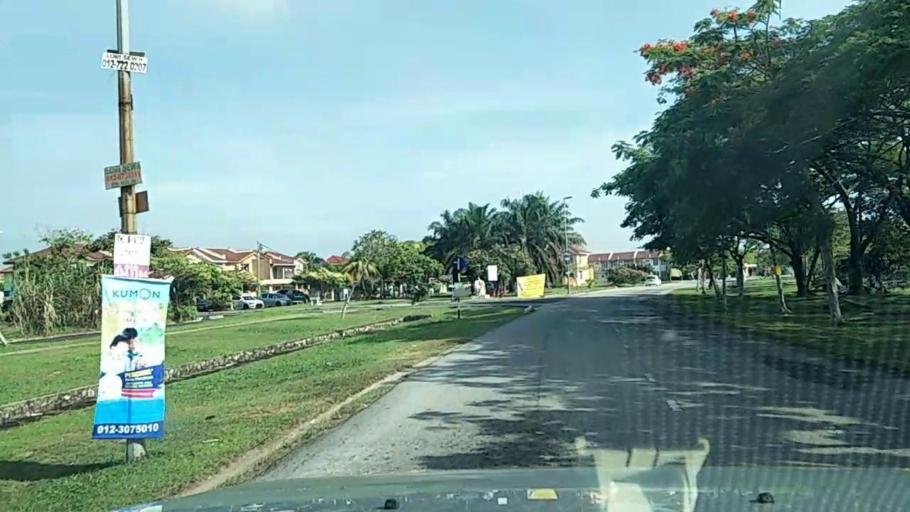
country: MY
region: Putrajaya
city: Putrajaya
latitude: 2.9427
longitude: 101.6192
